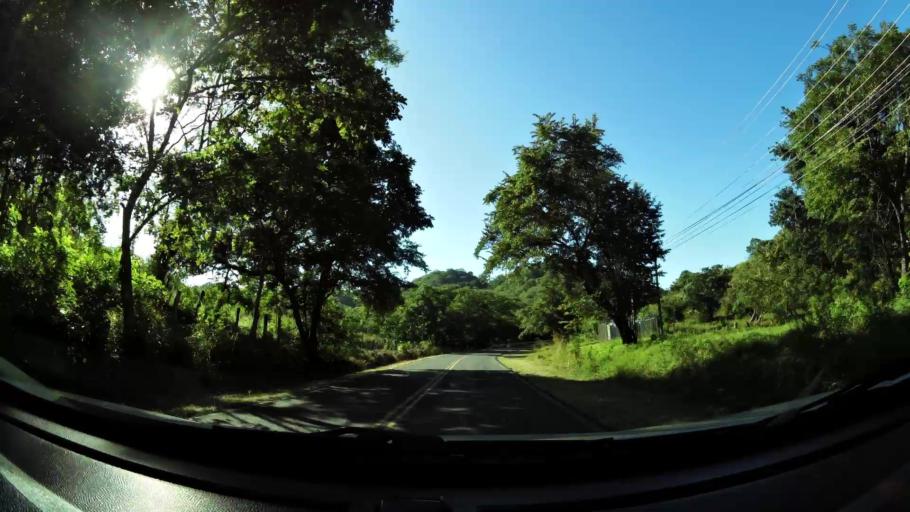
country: CR
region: Guanacaste
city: Belen
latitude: 10.3797
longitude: -85.6209
